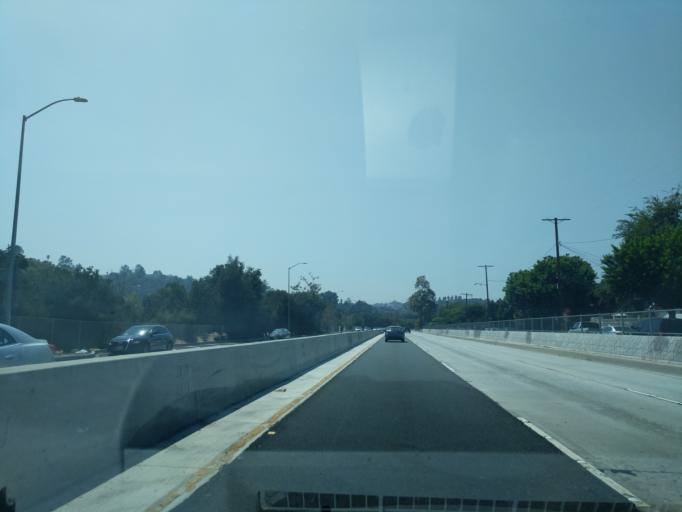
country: US
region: California
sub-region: Los Angeles County
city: South Pasadena
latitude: 34.1161
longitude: -118.1714
